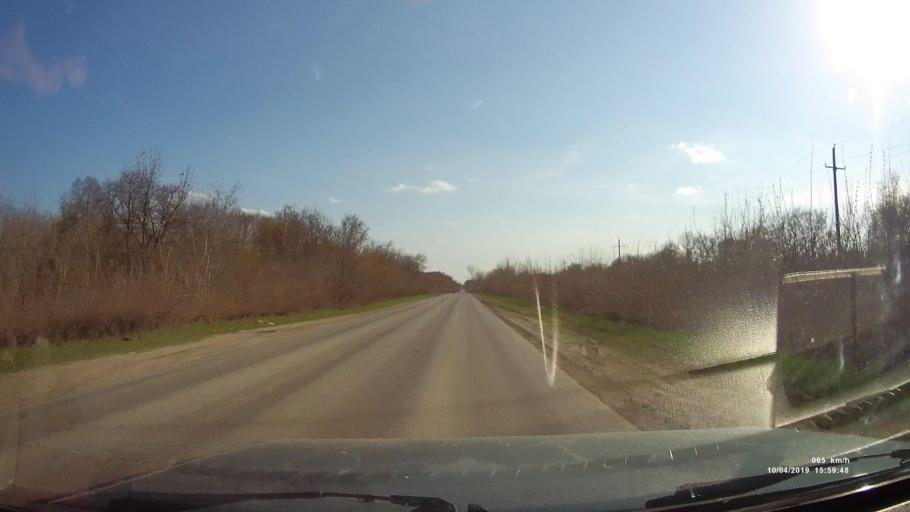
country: RU
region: Rostov
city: Masalovka
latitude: 48.3909
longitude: 40.2668
